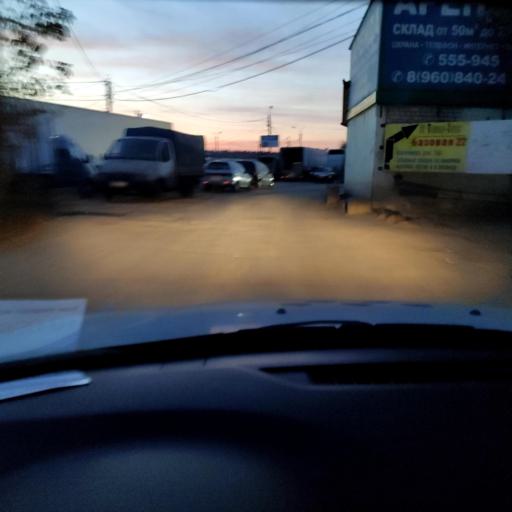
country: RU
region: Samara
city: Zhigulevsk
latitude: 53.5211
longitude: 49.4738
